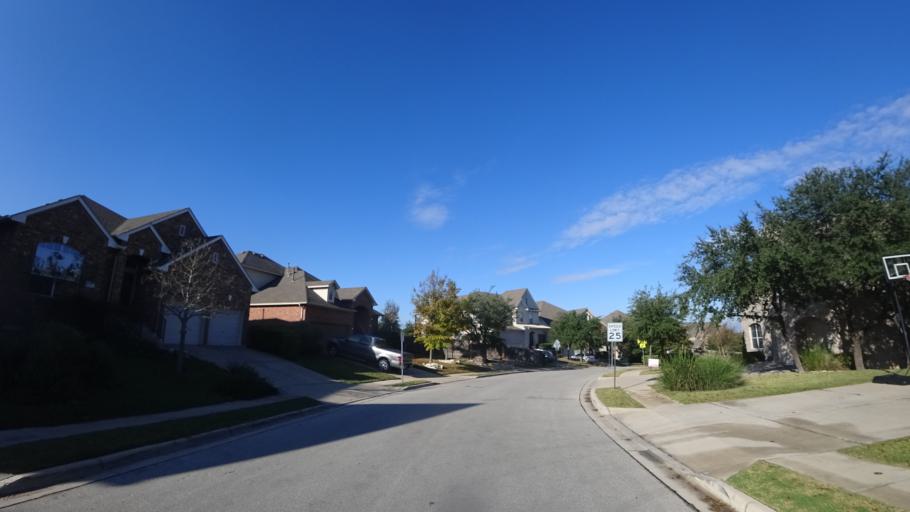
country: US
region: Texas
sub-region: Travis County
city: Hudson Bend
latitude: 30.3672
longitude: -97.8976
